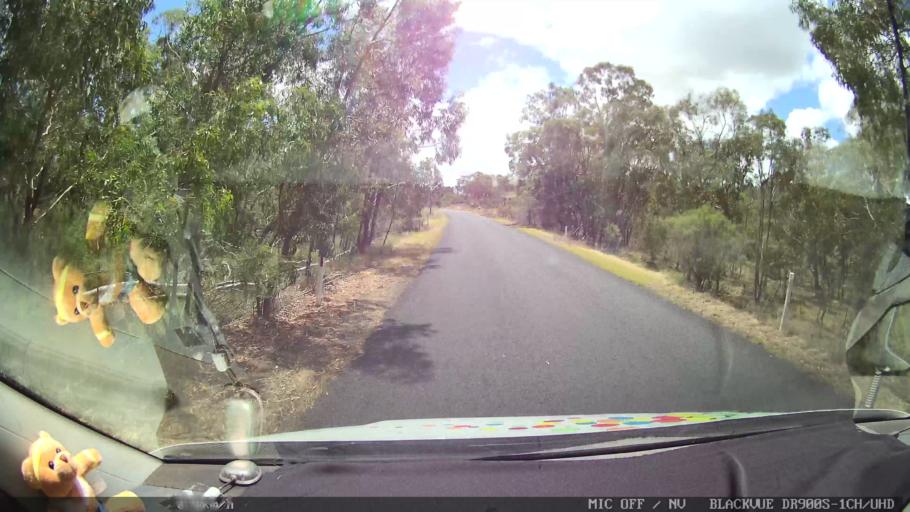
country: AU
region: New South Wales
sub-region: Glen Innes Severn
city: Glen Innes
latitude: -29.4314
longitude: 151.7902
